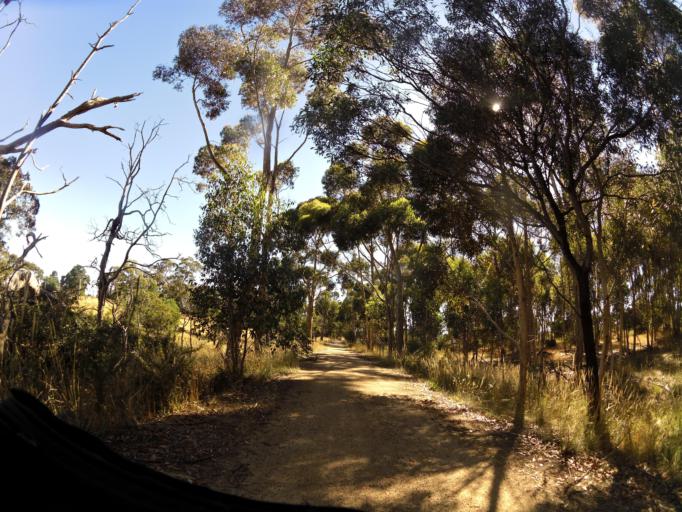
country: AU
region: Victoria
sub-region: Ballarat North
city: Delacombe
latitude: -37.6784
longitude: 143.4388
